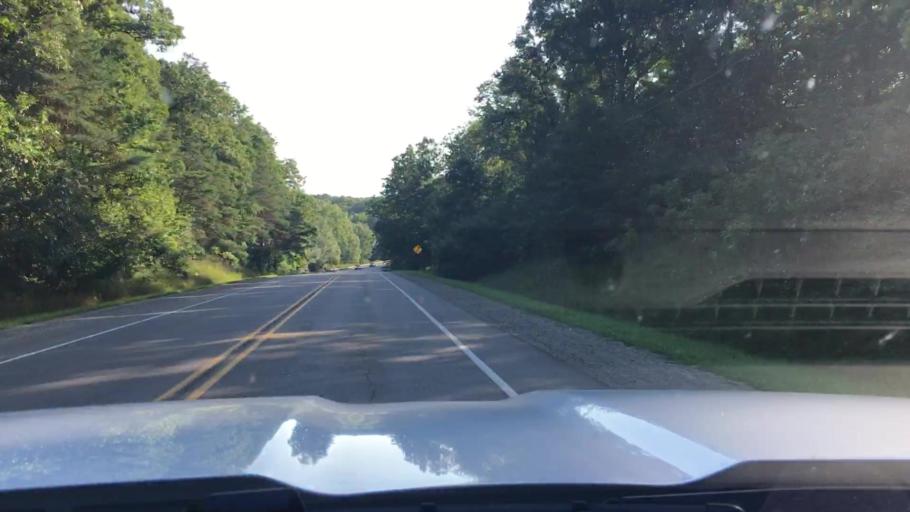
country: US
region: Michigan
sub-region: Kent County
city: Lowell
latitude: 42.9052
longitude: -85.3656
